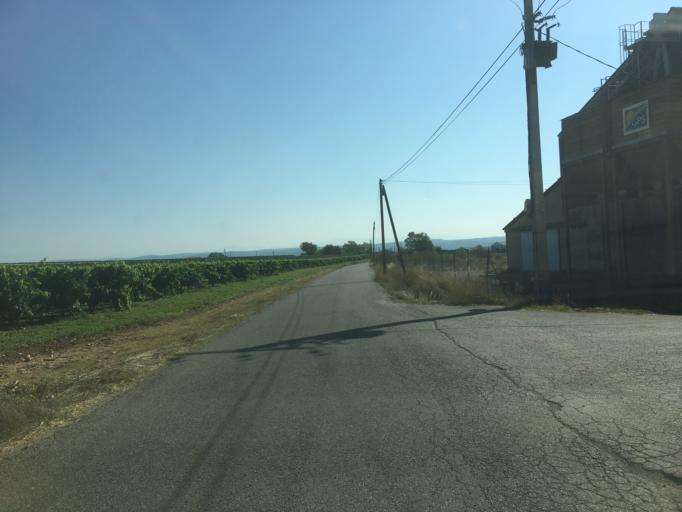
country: FR
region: Provence-Alpes-Cote d'Azur
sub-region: Departement des Alpes-de-Haute-Provence
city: Sainte-Tulle
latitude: 43.7981
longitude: 5.7779
